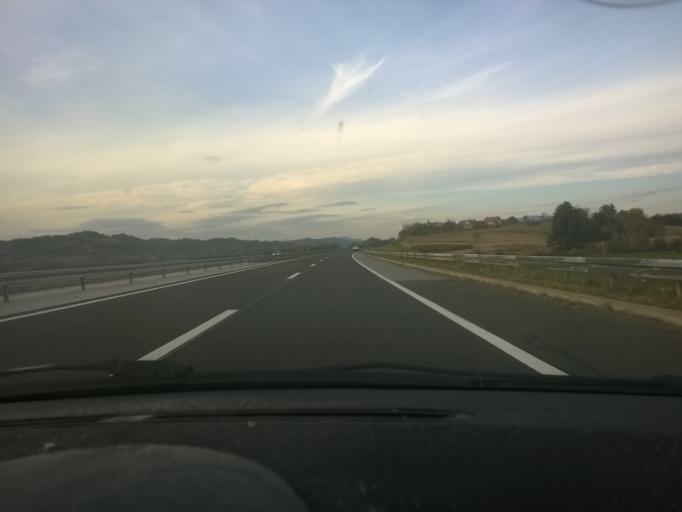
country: HR
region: Krapinsko-Zagorska
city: Zabok
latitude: 46.0519
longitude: 15.9207
